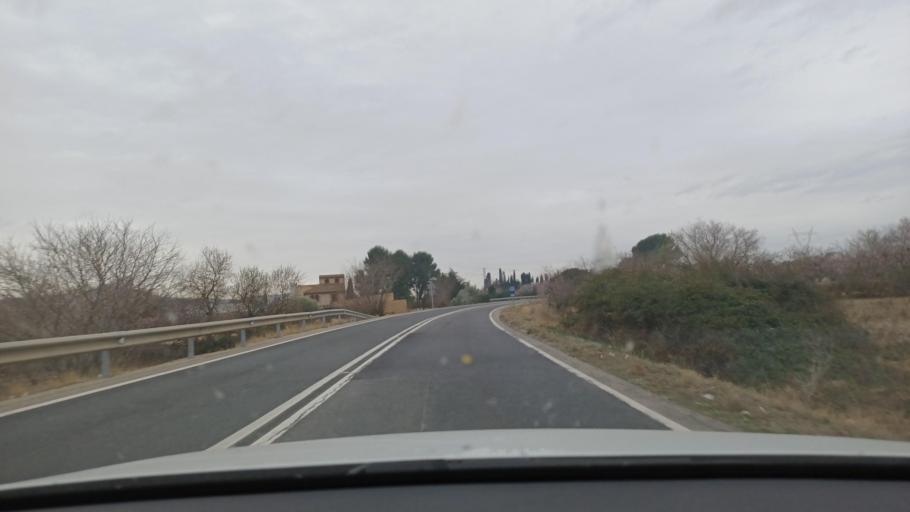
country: ES
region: Catalonia
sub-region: Provincia de Tarragona
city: Santa Barbara
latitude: 40.6842
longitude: 0.4625
